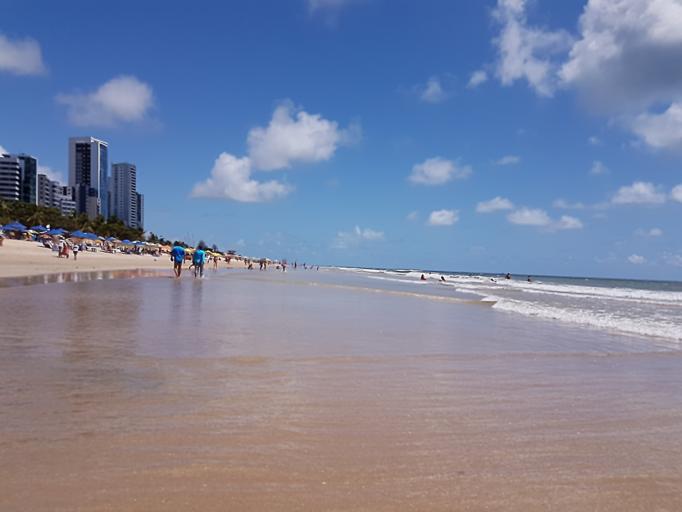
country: BR
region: Pernambuco
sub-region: Recife
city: Recife
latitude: -8.1031
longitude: -34.8850
